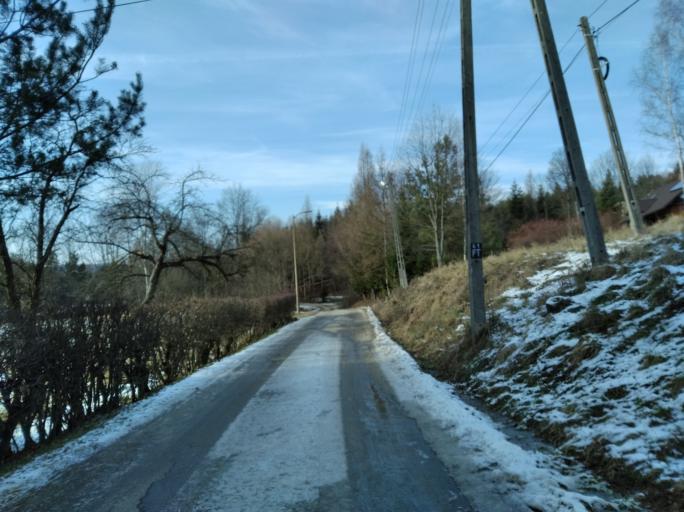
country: PL
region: Subcarpathian Voivodeship
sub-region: Powiat krosnienski
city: Korczyna
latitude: 49.7688
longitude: 21.7973
